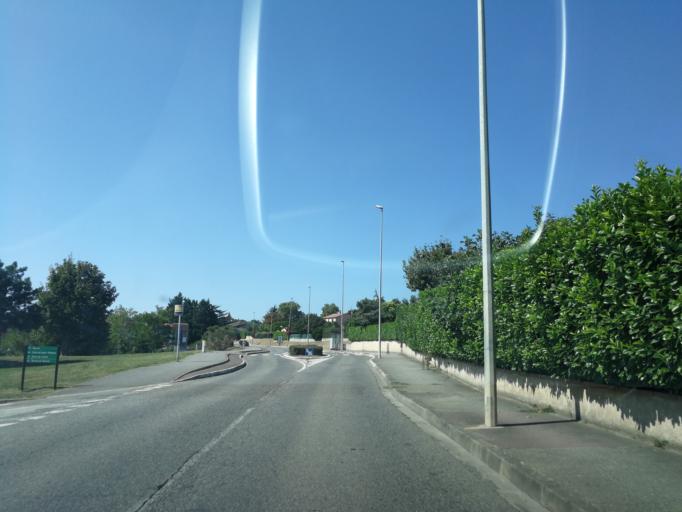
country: FR
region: Midi-Pyrenees
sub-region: Departement de la Haute-Garonne
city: Saint-Orens-de-Gameville
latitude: 43.5828
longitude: 1.5344
